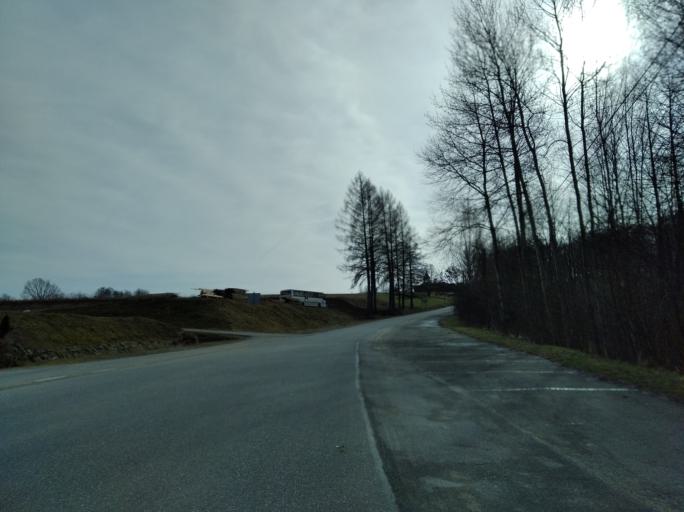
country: PL
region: Subcarpathian Voivodeship
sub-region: Powiat brzozowski
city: Jasienica Rosielna
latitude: 49.7483
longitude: 21.9412
